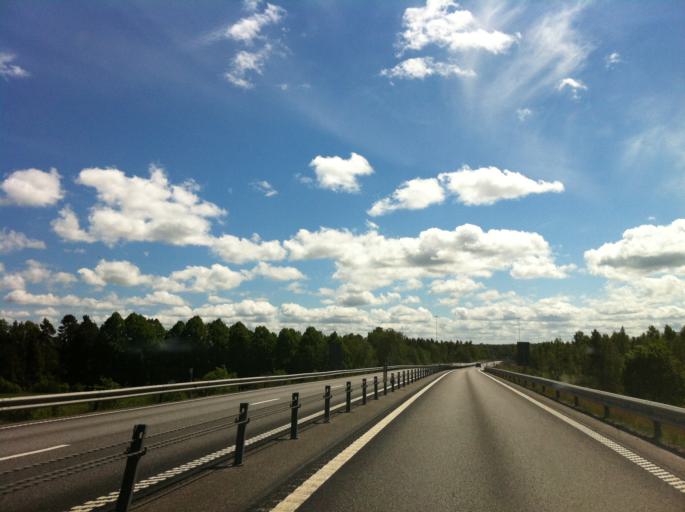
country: SE
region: Vaestra Goetaland
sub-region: Vanersborgs Kommun
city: Vanersborg
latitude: 58.3567
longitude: 12.2580
